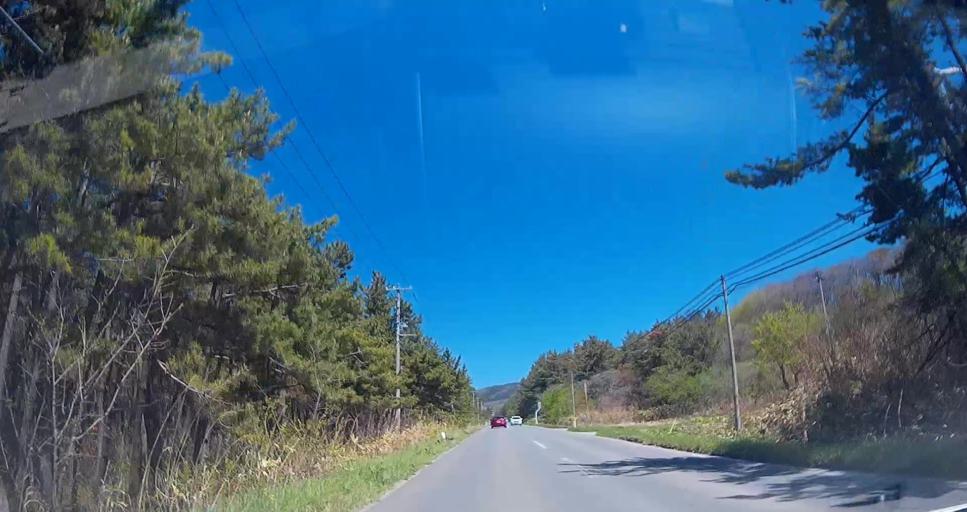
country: JP
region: Aomori
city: Mutsu
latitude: 41.3751
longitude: 141.3903
